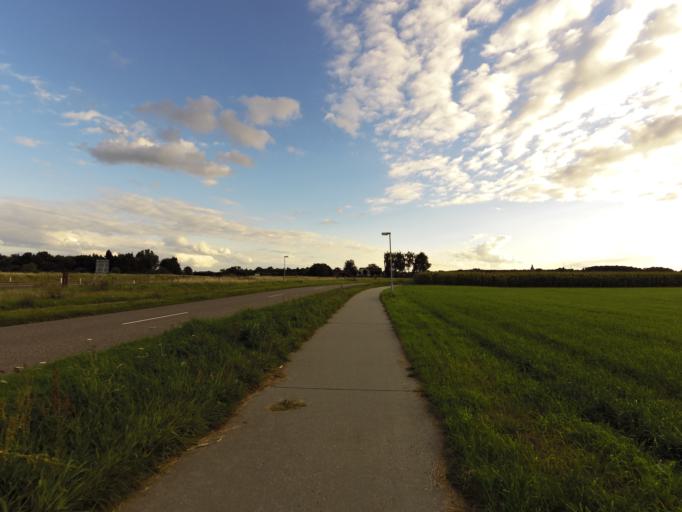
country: NL
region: Gelderland
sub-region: Gemeente Montferland
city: s-Heerenberg
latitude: 51.9136
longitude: 6.2645
